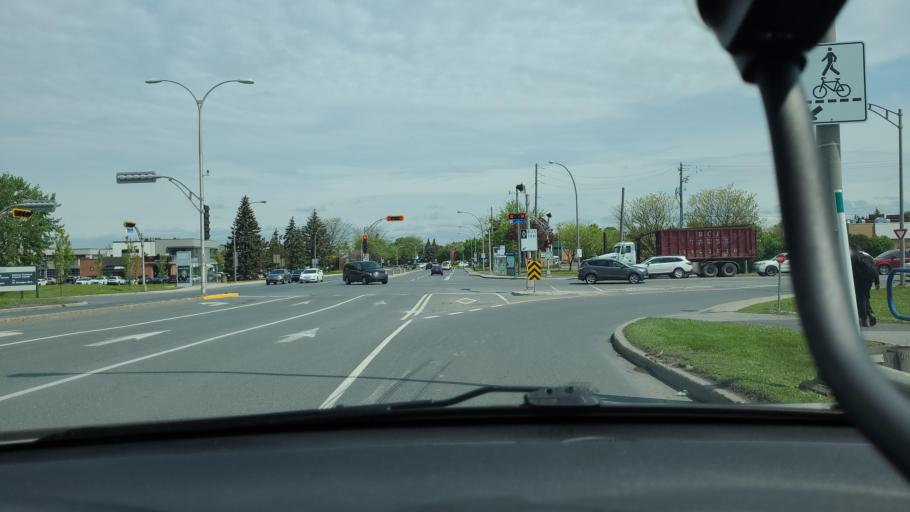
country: CA
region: Quebec
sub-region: Monteregie
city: Boucherville
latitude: 45.5736
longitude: -73.4472
